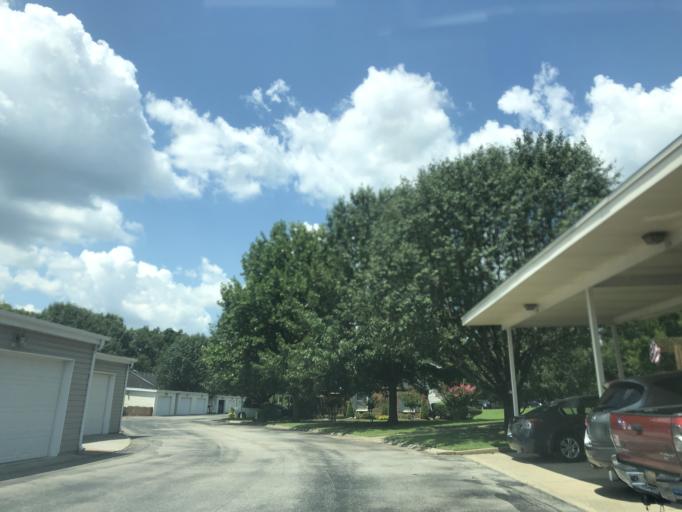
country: US
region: Tennessee
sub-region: Wilson County
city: Green Hill
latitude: 36.1611
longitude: -86.5947
